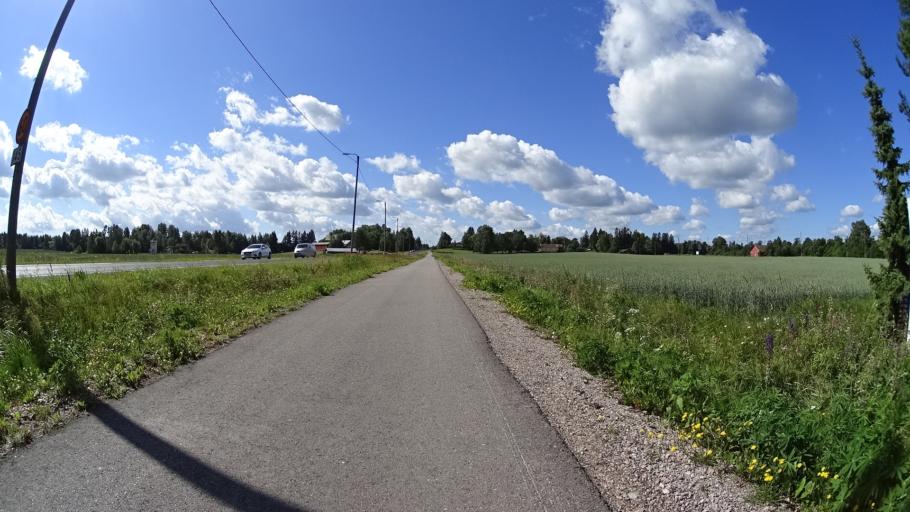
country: FI
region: Uusimaa
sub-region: Helsinki
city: Jaervenpaeae
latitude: 60.4425
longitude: 25.0746
